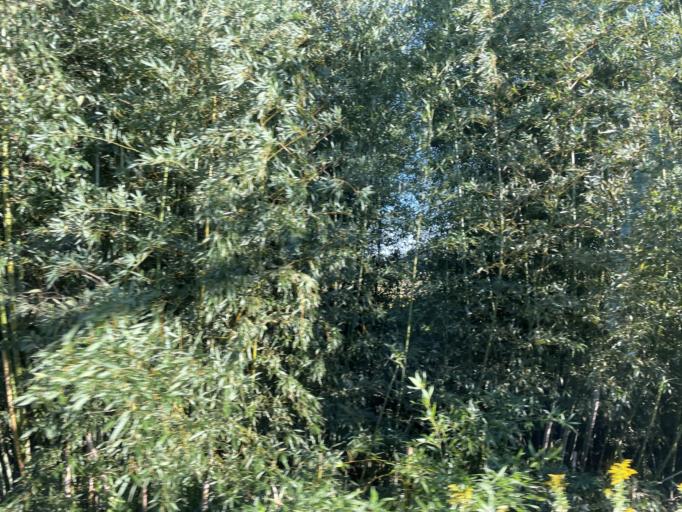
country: JP
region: Tochigi
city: Fujioka
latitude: 36.3183
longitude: 139.6868
